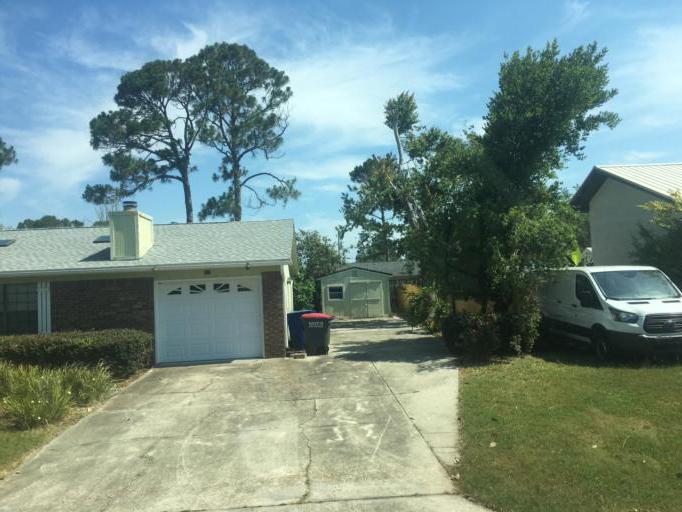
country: US
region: Florida
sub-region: Bay County
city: Lower Grand Lagoon
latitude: 30.1640
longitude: -85.7658
